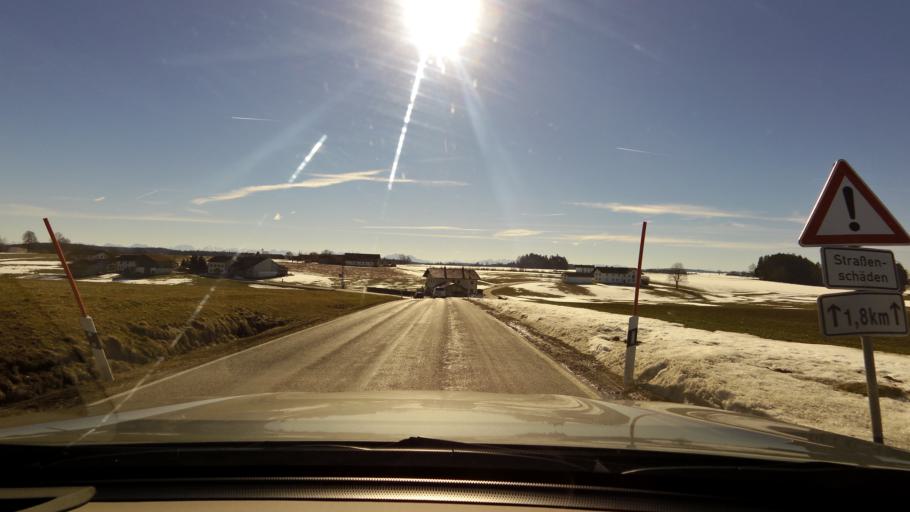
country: DE
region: Bavaria
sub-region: Upper Bavaria
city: Taufkirchen
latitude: 48.1121
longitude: 12.4692
